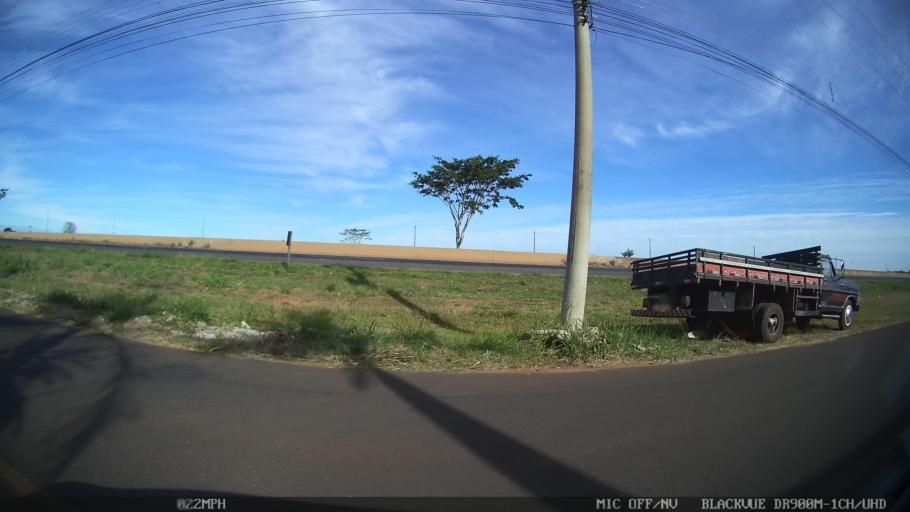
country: BR
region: Sao Paulo
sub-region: Sao Jose Do Rio Preto
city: Sao Jose do Rio Preto
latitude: -20.7924
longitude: -49.3045
